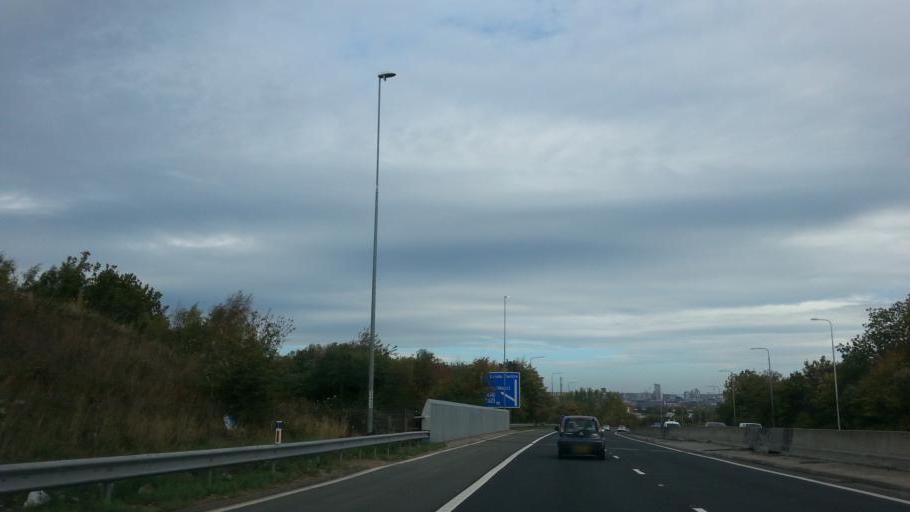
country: GB
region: England
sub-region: City and Borough of Leeds
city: Morley
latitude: 53.7705
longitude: -1.5900
